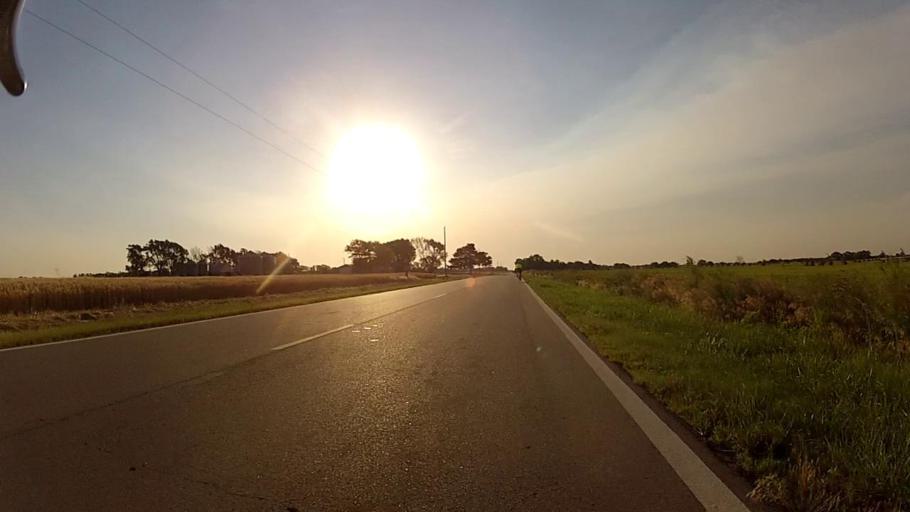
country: US
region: Kansas
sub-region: Harper County
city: Anthony
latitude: 37.1538
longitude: -97.8535
